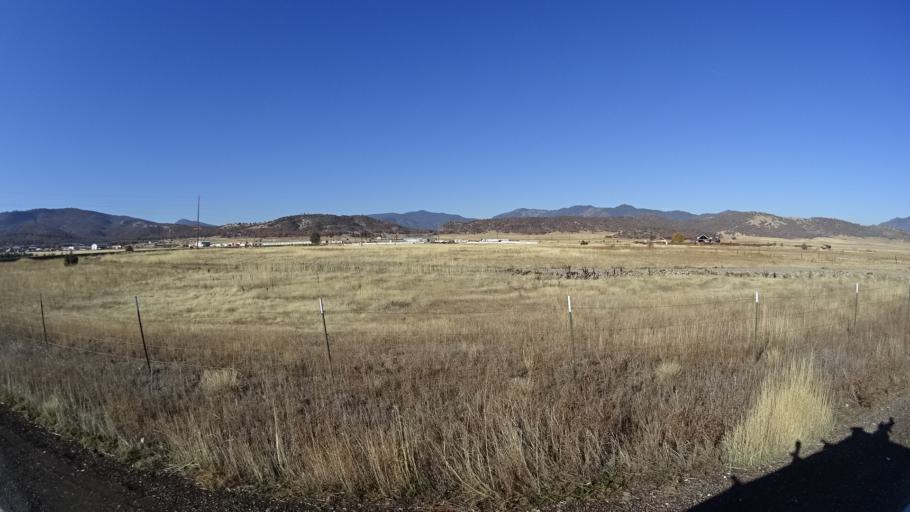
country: US
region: California
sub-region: Siskiyou County
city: Yreka
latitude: 41.7123
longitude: -122.5937
